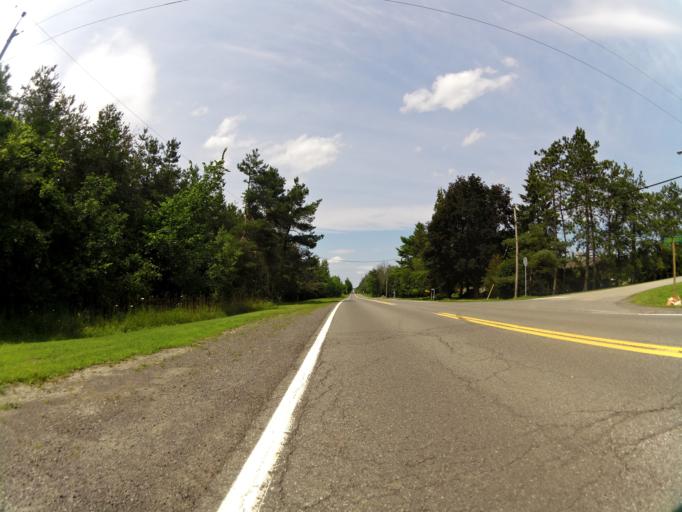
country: CA
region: Ontario
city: Ottawa
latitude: 45.2804
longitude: -75.6286
